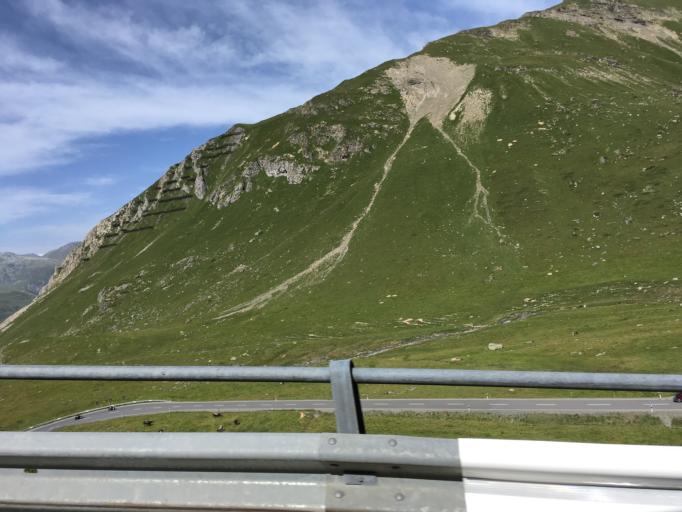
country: CH
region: Grisons
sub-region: Maloja District
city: Silvaplana
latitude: 46.4706
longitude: 9.7168
